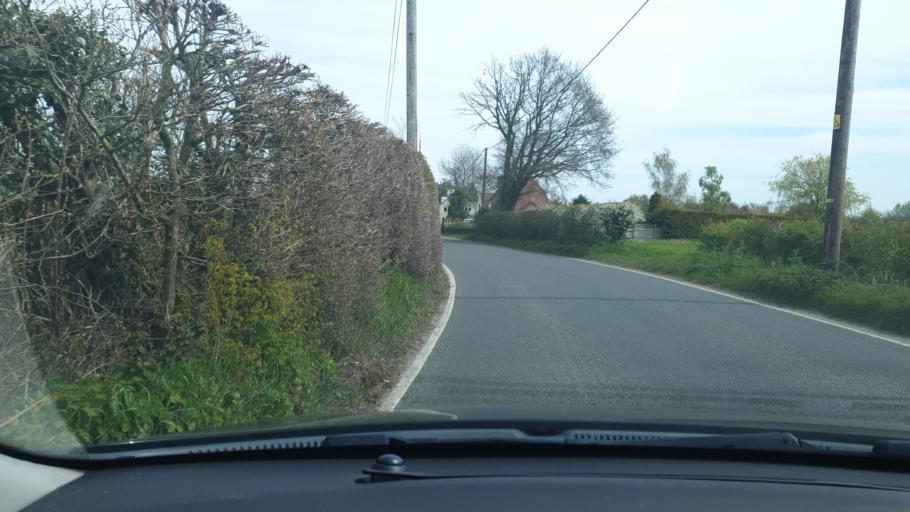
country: GB
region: England
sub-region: Essex
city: Mistley
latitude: 51.9116
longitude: 1.1551
